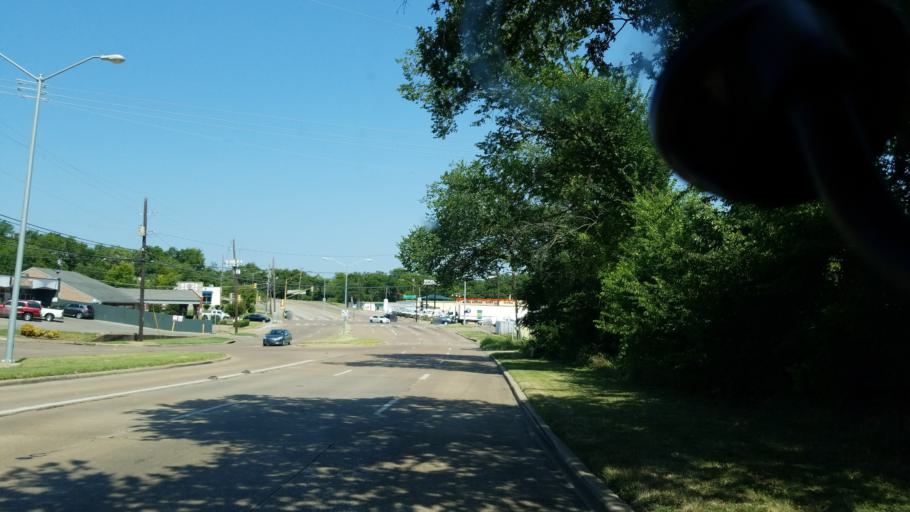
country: US
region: Texas
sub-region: Dallas County
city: Cockrell Hill
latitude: 32.7052
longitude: -96.8737
